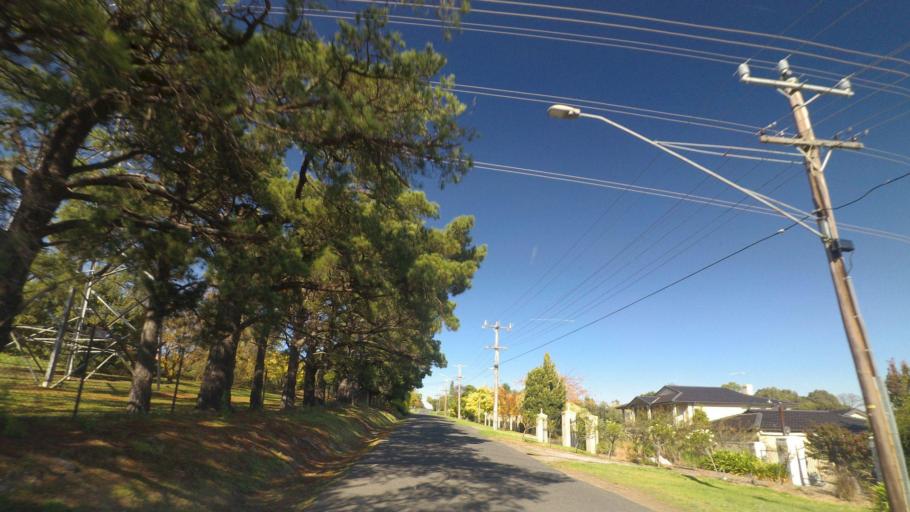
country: AU
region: Victoria
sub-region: Nillumbik
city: Eltham
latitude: -37.7447
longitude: 145.1588
